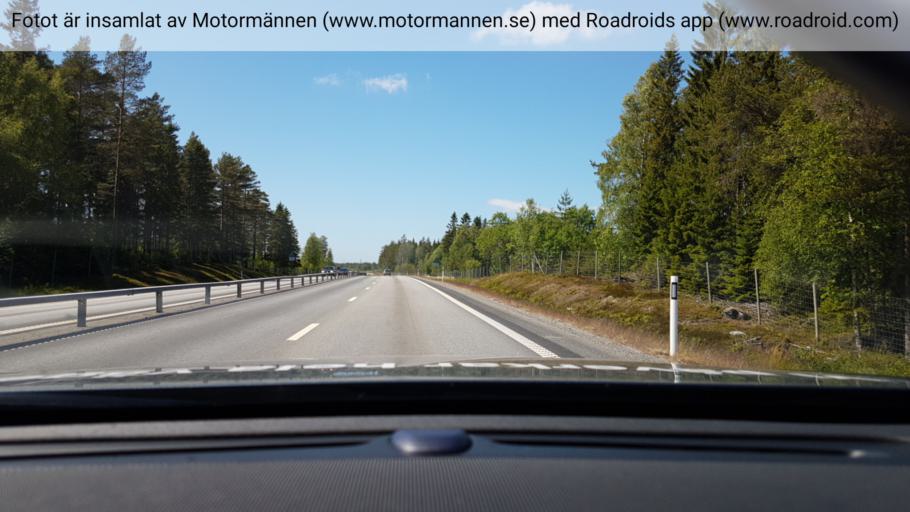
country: SE
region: Vaesterbotten
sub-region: Umea Kommun
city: Hoernefors
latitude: 63.6366
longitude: 19.9025
